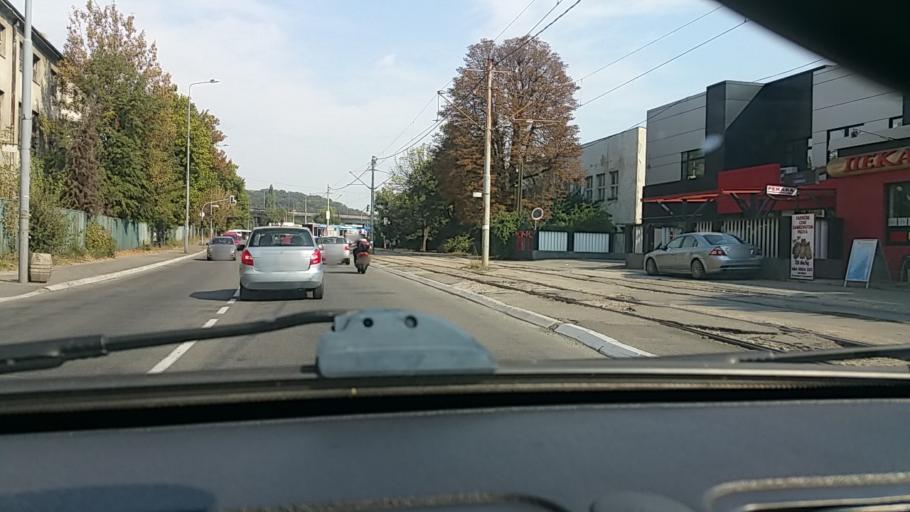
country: RS
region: Central Serbia
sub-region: Belgrade
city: Rakovica
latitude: 44.7420
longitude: 20.4409
